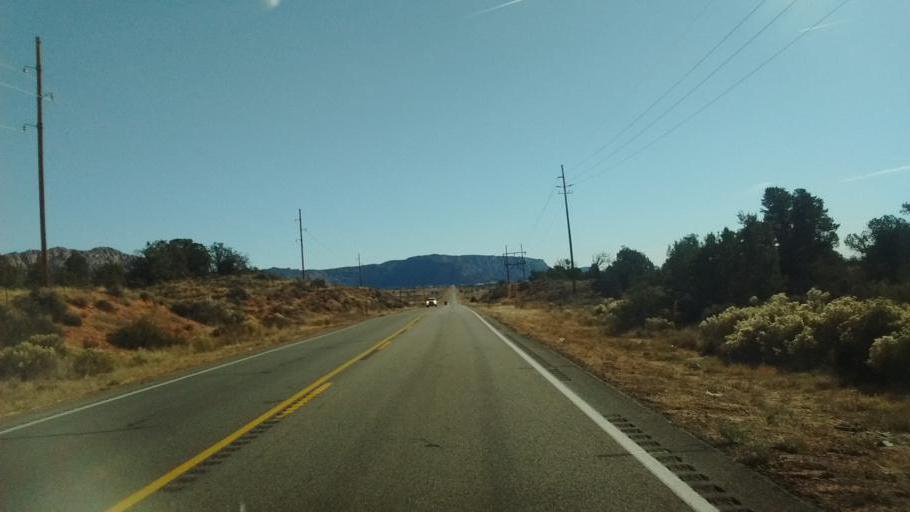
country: US
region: Arizona
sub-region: Mohave County
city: Colorado City
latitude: 37.0205
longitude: -113.0359
